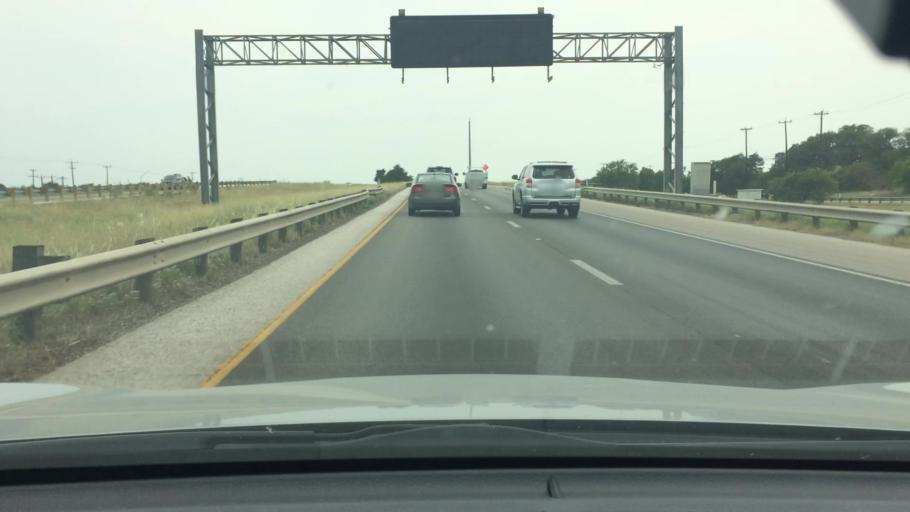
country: US
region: Texas
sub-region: Bexar County
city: Helotes
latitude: 29.5789
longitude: -98.6441
